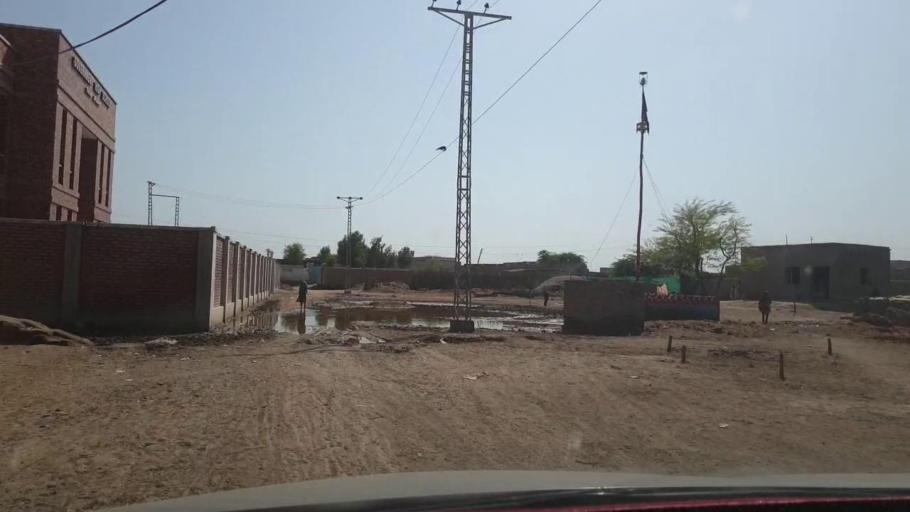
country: PK
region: Sindh
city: Nasirabad
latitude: 27.3451
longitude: 67.8401
